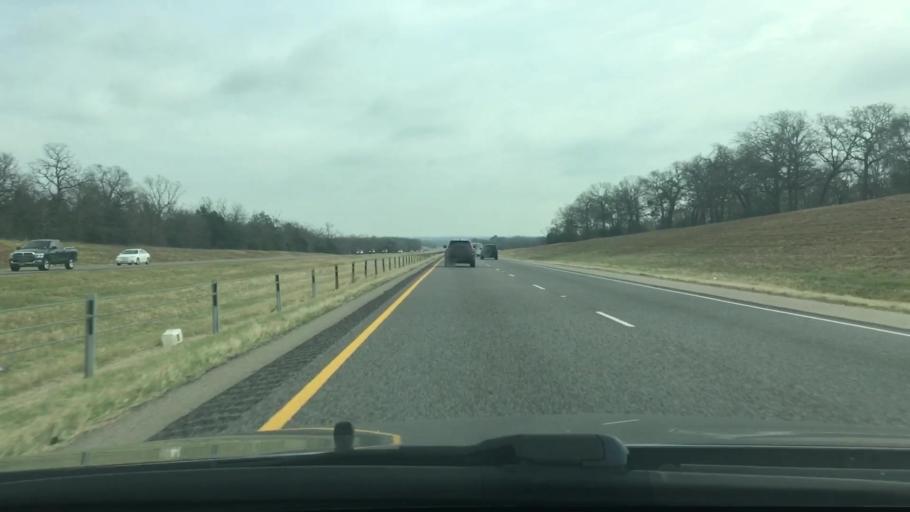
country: US
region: Texas
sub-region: Leon County
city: Buffalo
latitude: 31.5293
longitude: -96.1157
